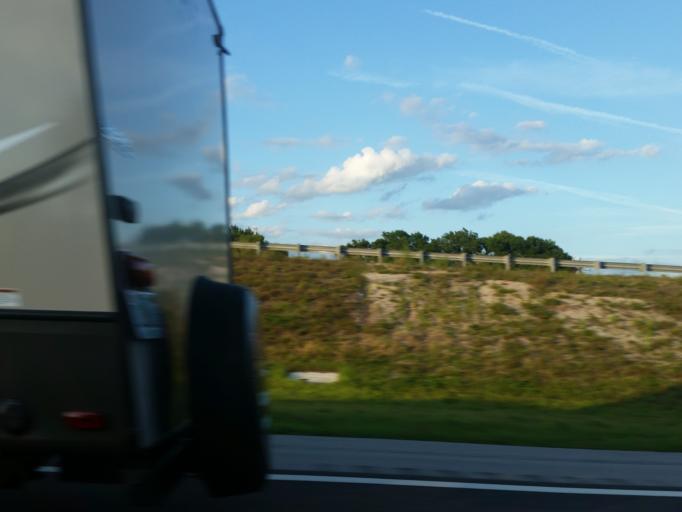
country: US
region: Florida
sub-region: Sarasota County
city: Nokomis
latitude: 27.1359
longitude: -82.4060
